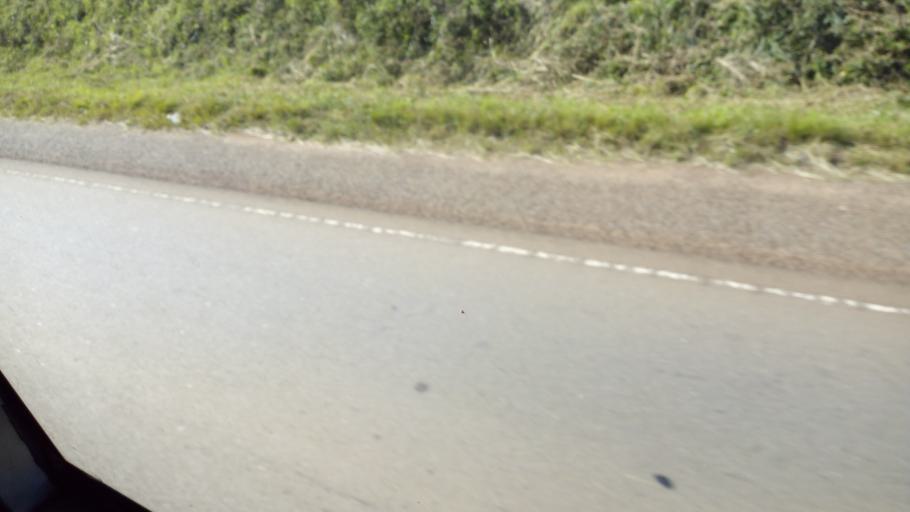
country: UG
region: Central Region
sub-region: Lyantonde District
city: Lyantonde
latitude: -0.4224
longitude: 31.1124
